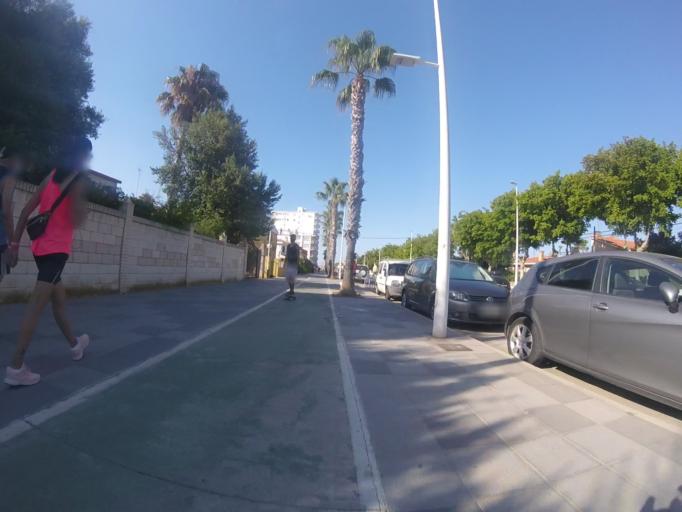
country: ES
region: Valencia
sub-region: Provincia de Castello
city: Benicarlo
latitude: 40.4026
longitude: 0.4185
